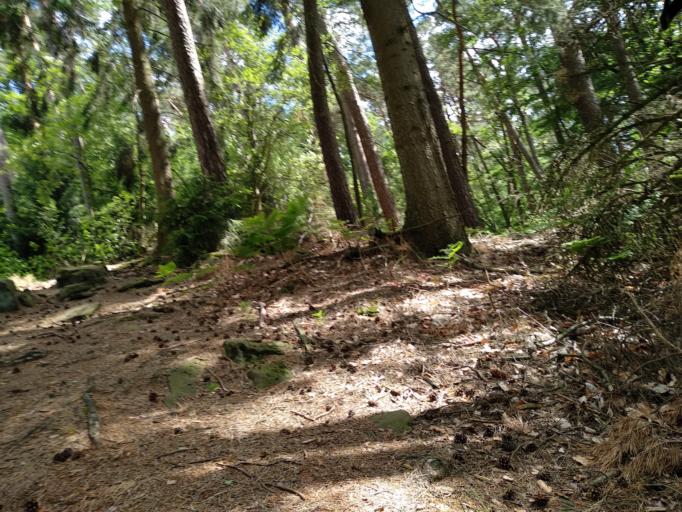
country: DE
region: Hesse
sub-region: Regierungsbezirk Giessen
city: Marburg an der Lahn
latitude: 50.8185
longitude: 8.7886
